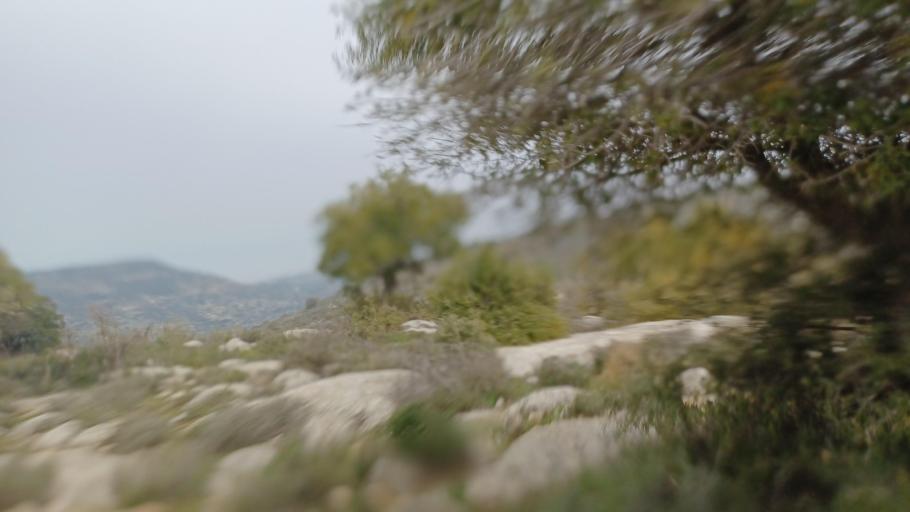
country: CY
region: Limassol
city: Pachna
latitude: 34.7543
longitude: 32.7446
